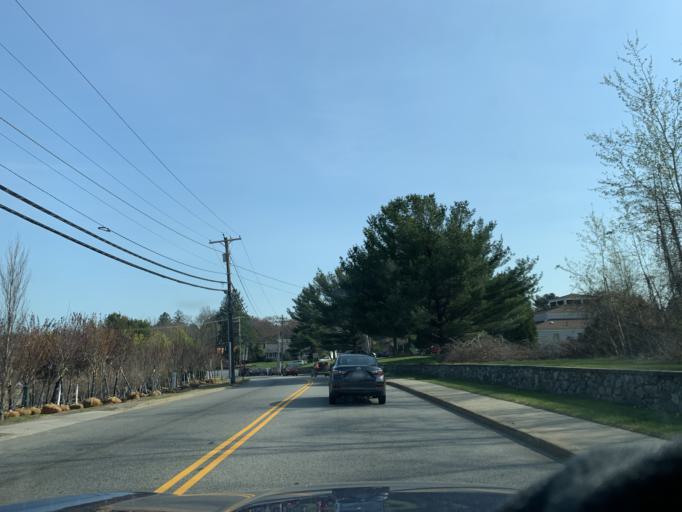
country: US
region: Rhode Island
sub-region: Providence County
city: Johnston
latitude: 41.7817
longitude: -71.5154
